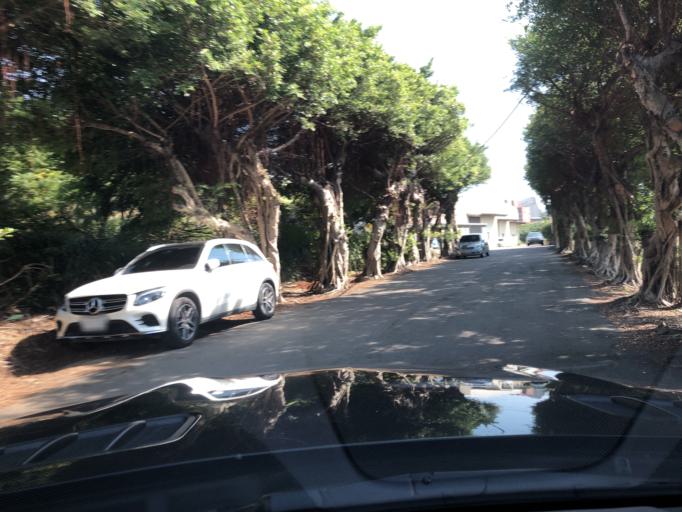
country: TW
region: Taiwan
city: Taoyuan City
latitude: 25.0655
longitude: 121.2913
